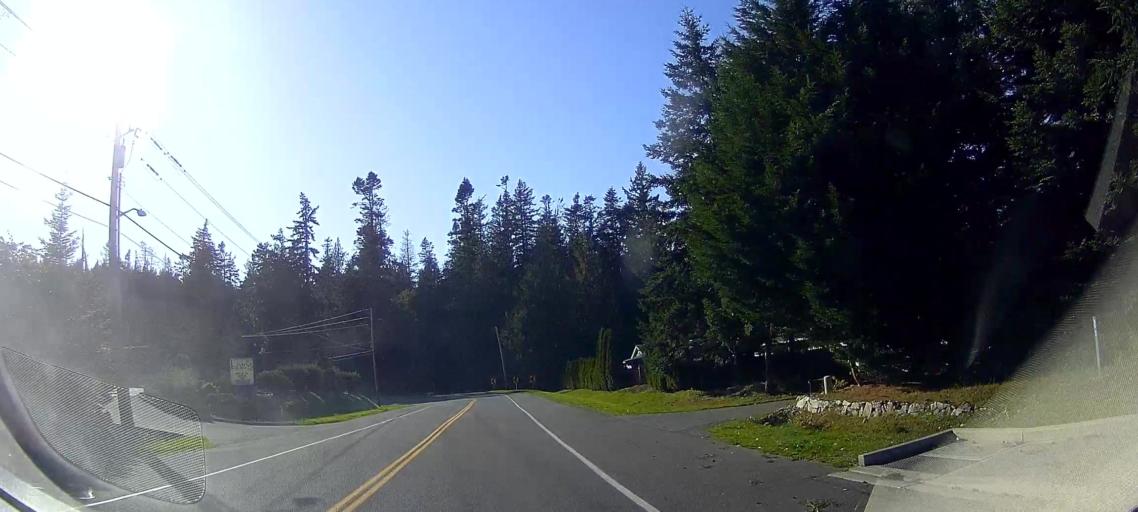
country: US
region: Washington
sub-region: Skagit County
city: Anacortes
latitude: 48.4924
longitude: -122.6348
